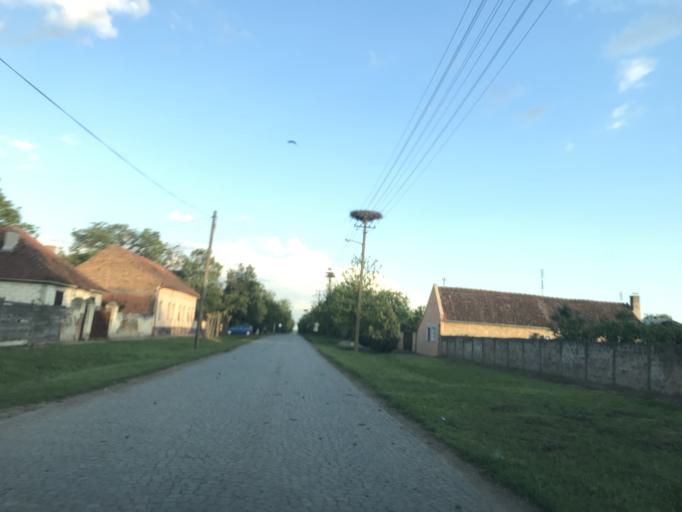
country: RS
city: Banatski Dvor
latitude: 45.5190
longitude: 20.5071
